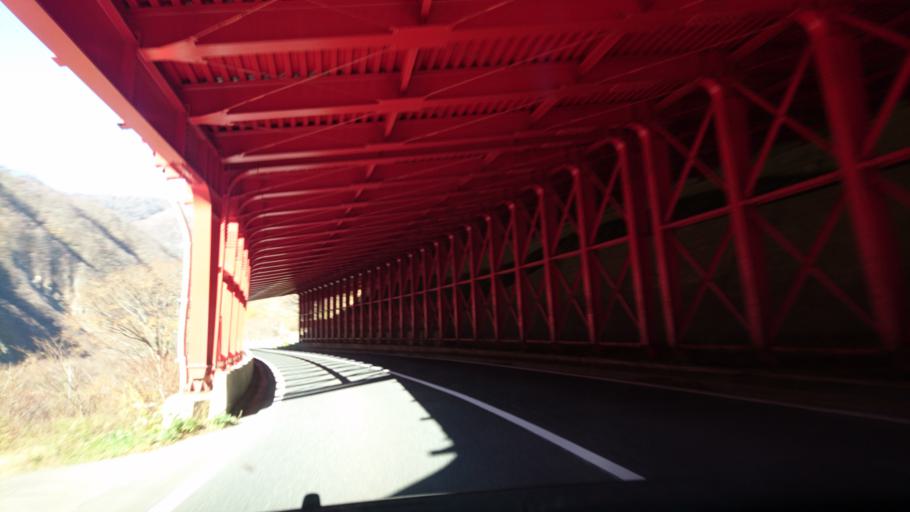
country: JP
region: Iwate
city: Kitakami
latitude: 39.3005
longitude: 140.8972
